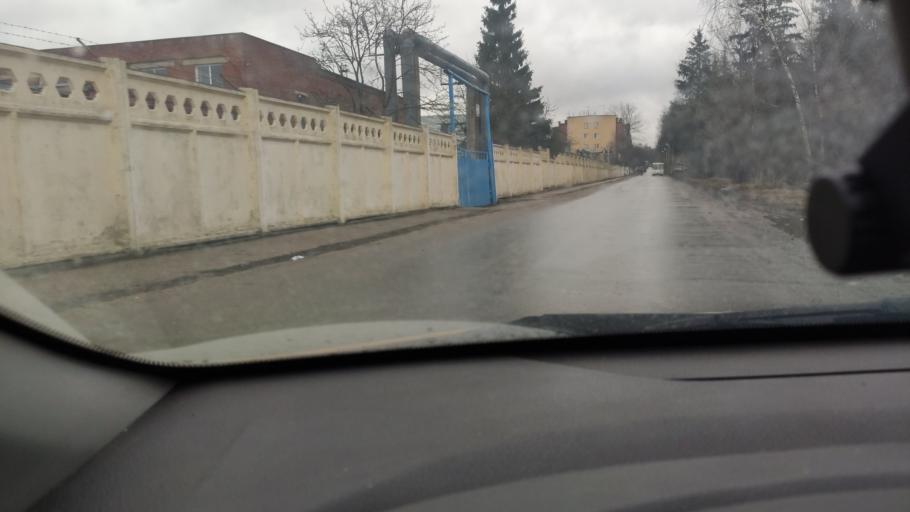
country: RU
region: Moskovskaya
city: Selyatino
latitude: 55.5131
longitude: 36.9663
